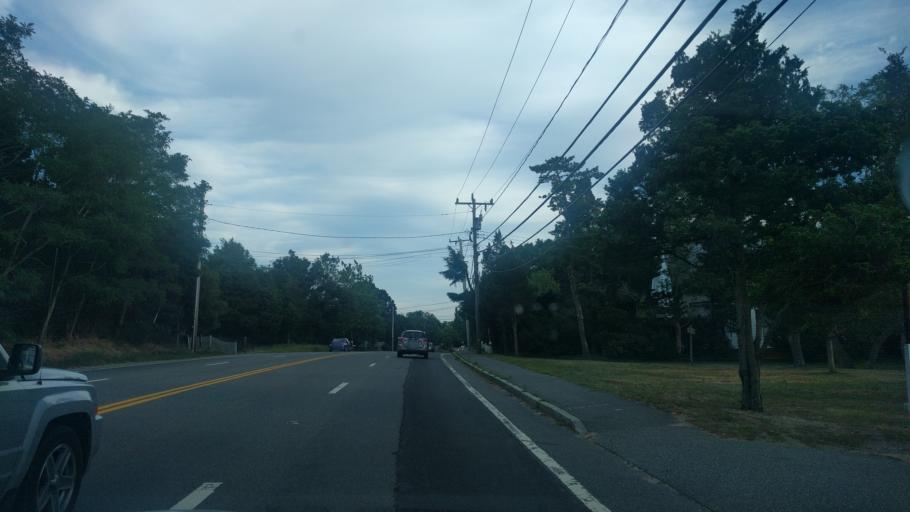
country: US
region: Massachusetts
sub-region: Barnstable County
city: Eastham
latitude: 41.8249
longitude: -69.9714
